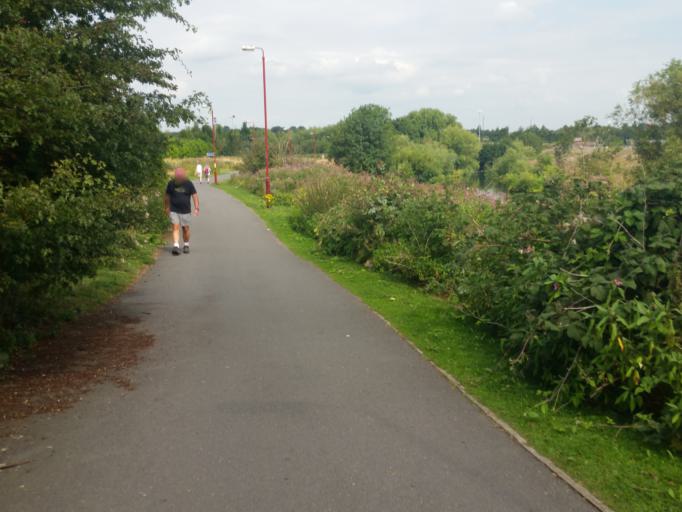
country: GB
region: England
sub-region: Derby
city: Derby
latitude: 52.9147
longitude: -1.4425
